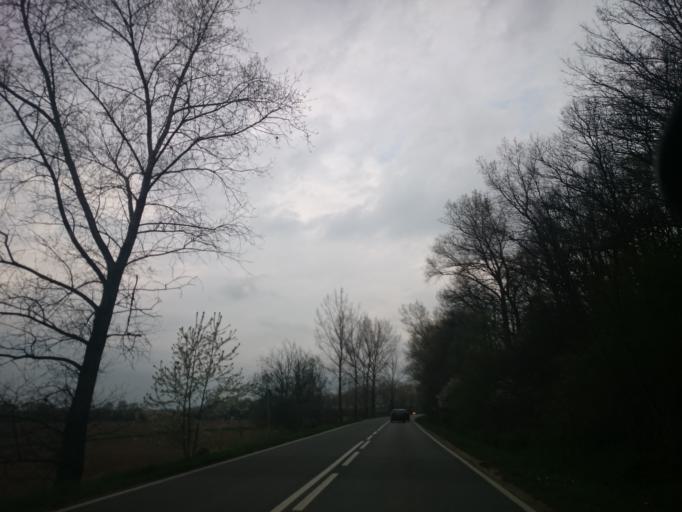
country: PL
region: Lower Silesian Voivodeship
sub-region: Powiat zabkowicki
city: Kamieniec Zabkowicki
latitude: 50.5365
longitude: 16.8643
